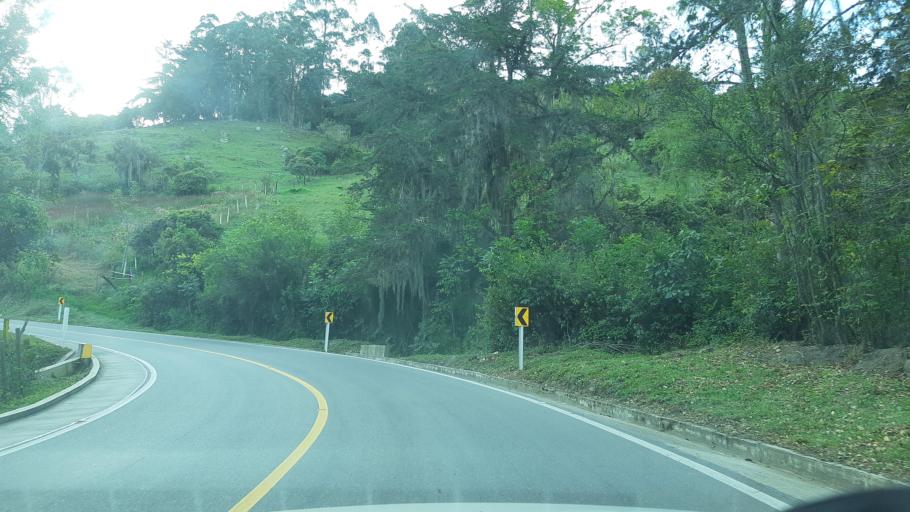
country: CO
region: Cundinamarca
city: Macheta
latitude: 5.0837
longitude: -73.6139
